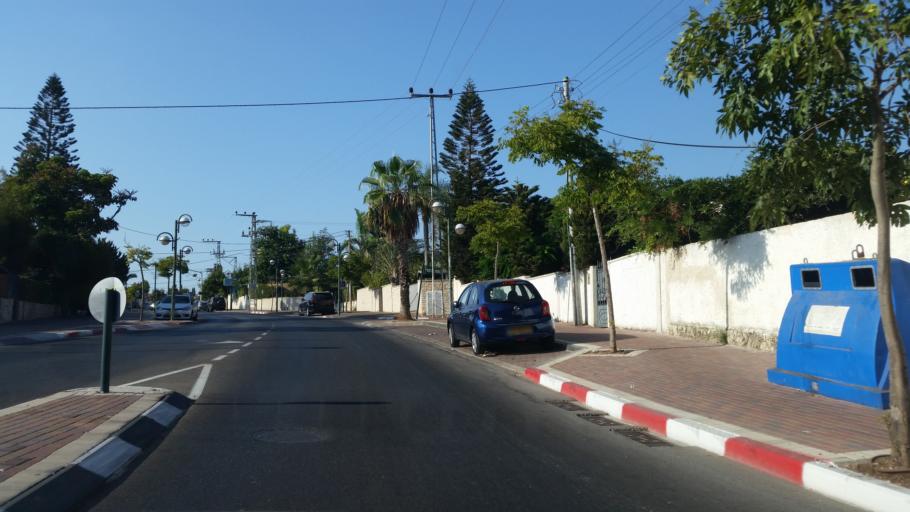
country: IL
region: Tel Aviv
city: Ramat HaSharon
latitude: 32.1316
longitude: 34.8531
